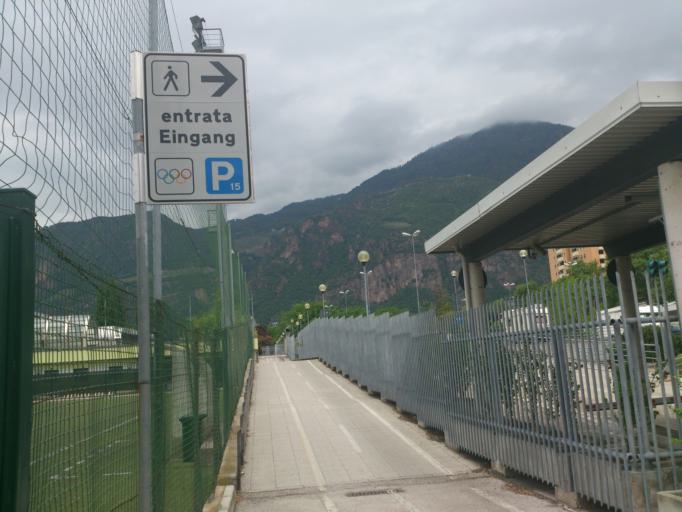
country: IT
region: Trentino-Alto Adige
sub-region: Bolzano
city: Bolzano
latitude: 46.4906
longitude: 11.3187
